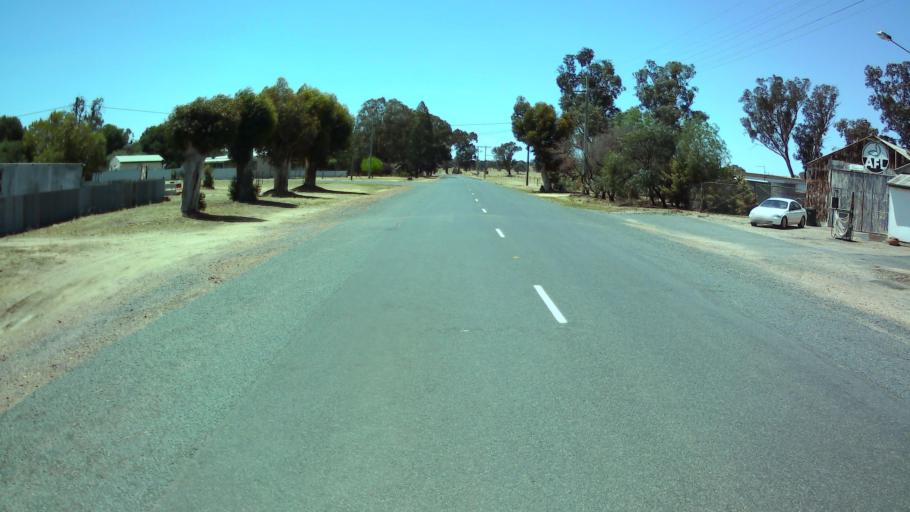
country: AU
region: New South Wales
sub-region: Weddin
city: Grenfell
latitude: -33.9946
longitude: 148.4047
